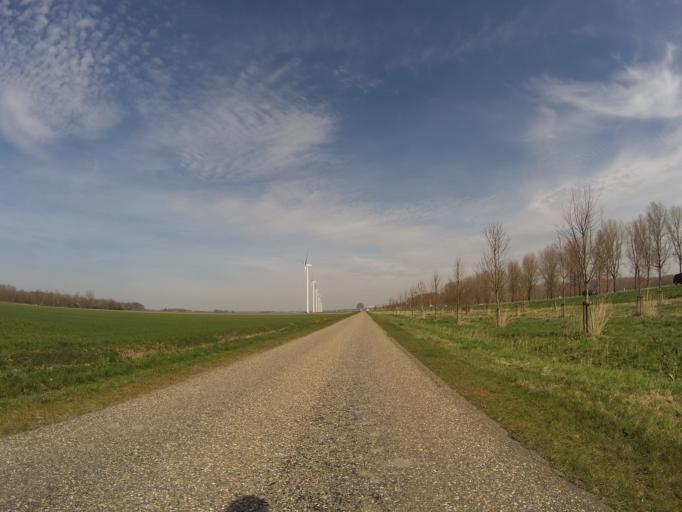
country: NL
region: Gelderland
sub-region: Gemeente Nijkerk
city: Nijkerk
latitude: 52.2775
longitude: 5.4630
